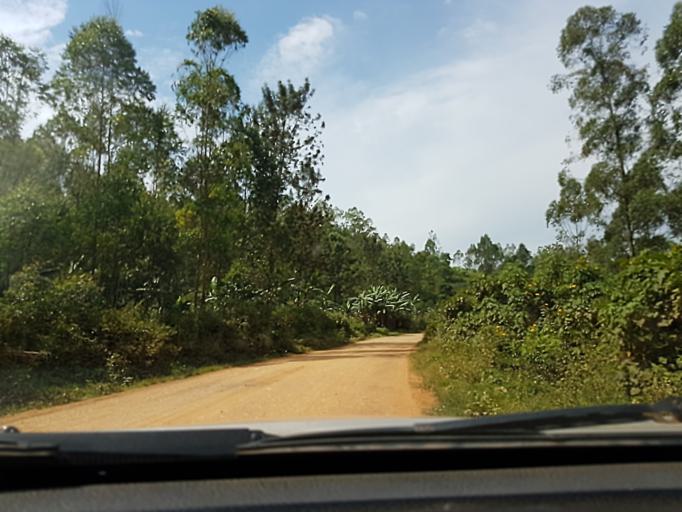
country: CD
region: South Kivu
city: Bukavu
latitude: -2.6439
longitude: 28.8777
